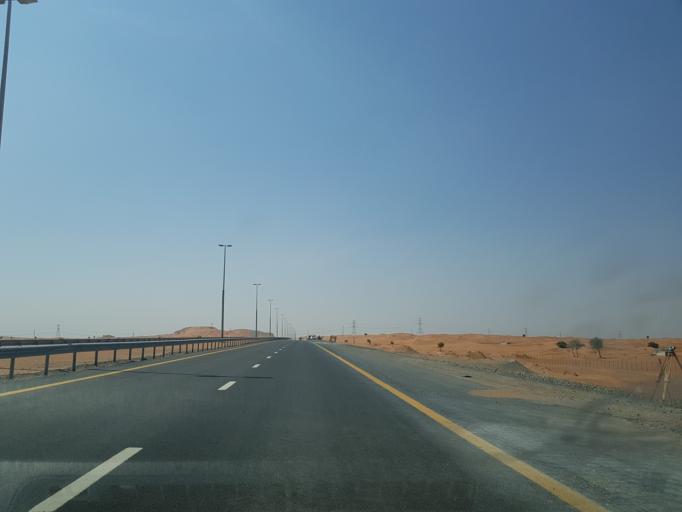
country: AE
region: Ash Shariqah
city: Adh Dhayd
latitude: 25.2439
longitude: 55.8626
